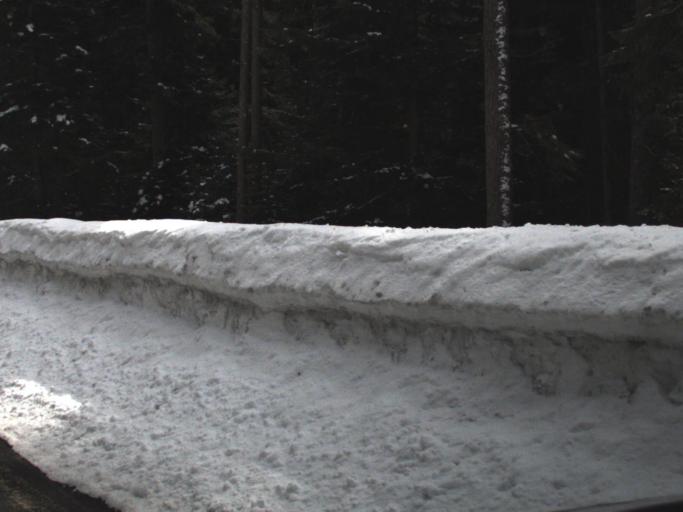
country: US
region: Washington
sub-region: Kittitas County
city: Cle Elum
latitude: 46.9138
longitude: -121.4050
